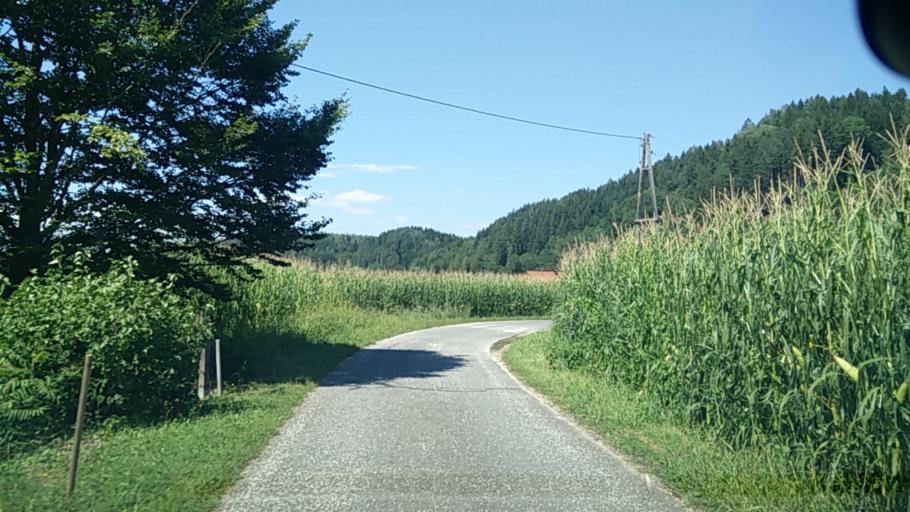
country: AT
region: Carinthia
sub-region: Politischer Bezirk Volkermarkt
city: Sittersdorf
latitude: 46.5467
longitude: 14.5883
